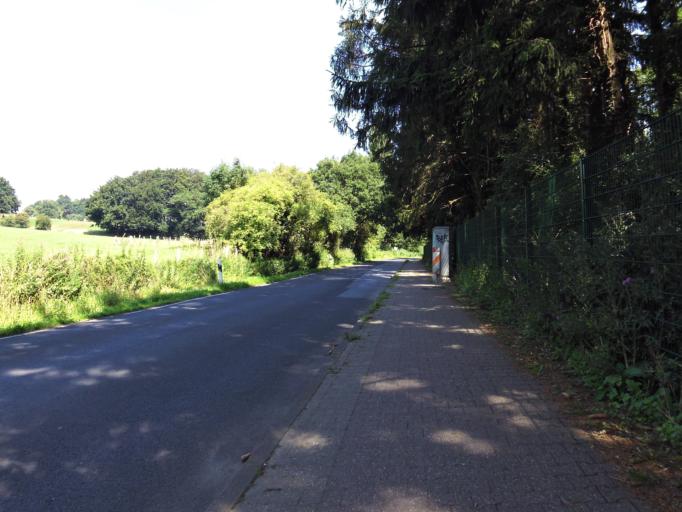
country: NL
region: Limburg
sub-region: Gemeente Vaals
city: Vaals
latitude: 50.7937
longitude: 6.0484
